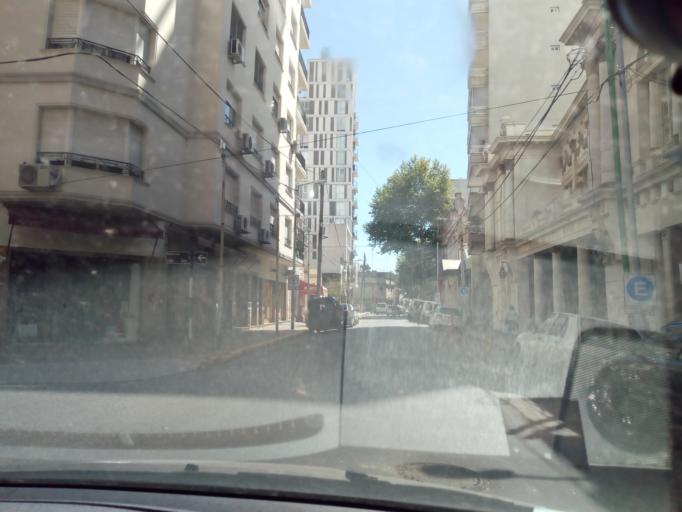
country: AR
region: Buenos Aires
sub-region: Partido de Avellaneda
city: Avellaneda
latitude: -34.6623
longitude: -58.3634
